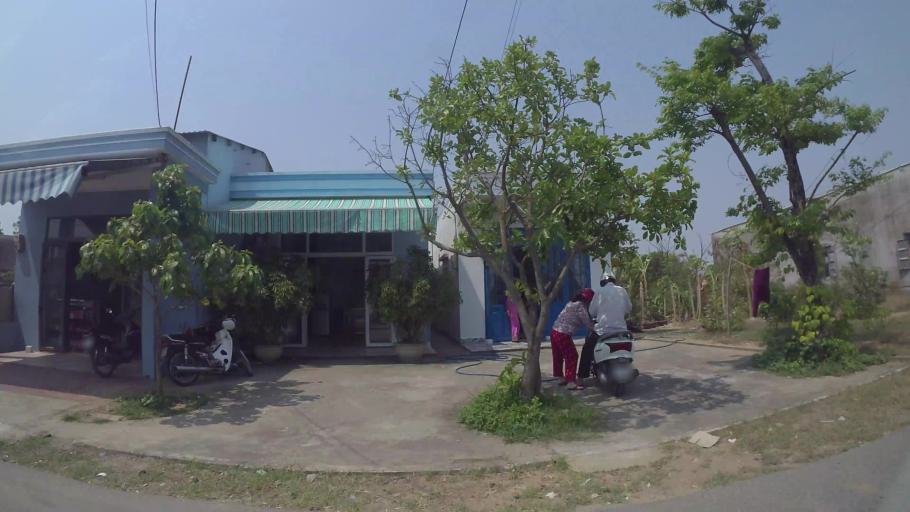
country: VN
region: Da Nang
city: Ngu Hanh Son
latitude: 16.0072
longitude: 108.2531
